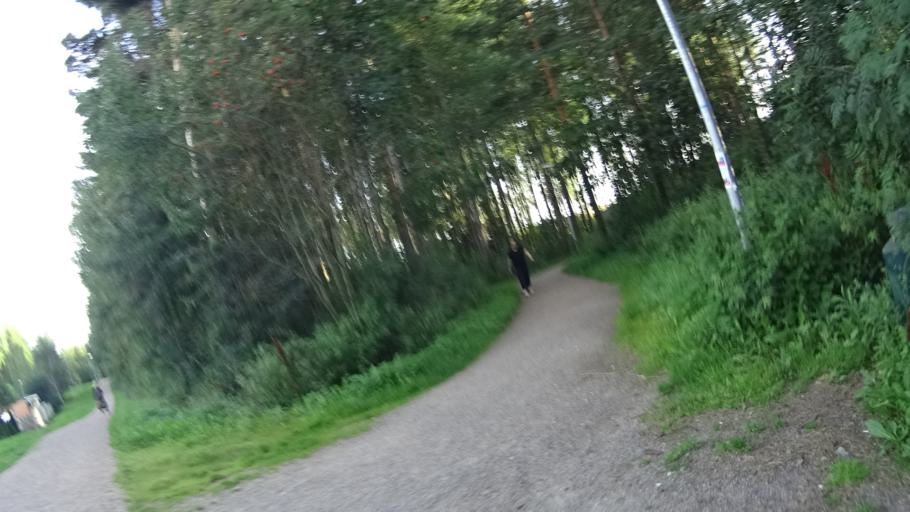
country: FI
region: Uusimaa
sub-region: Helsinki
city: Teekkarikylae
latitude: 60.2472
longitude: 24.8478
